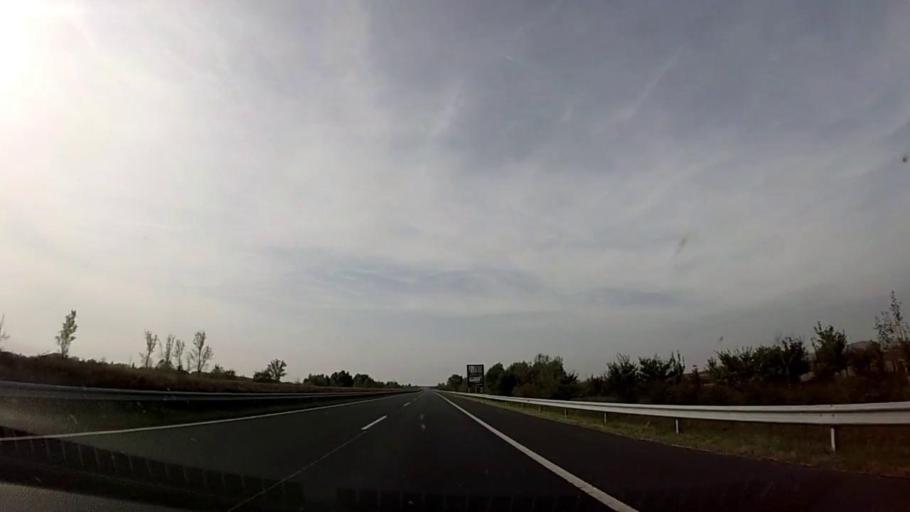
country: HU
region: Somogy
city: Fonyod
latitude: 46.7392
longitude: 17.6041
